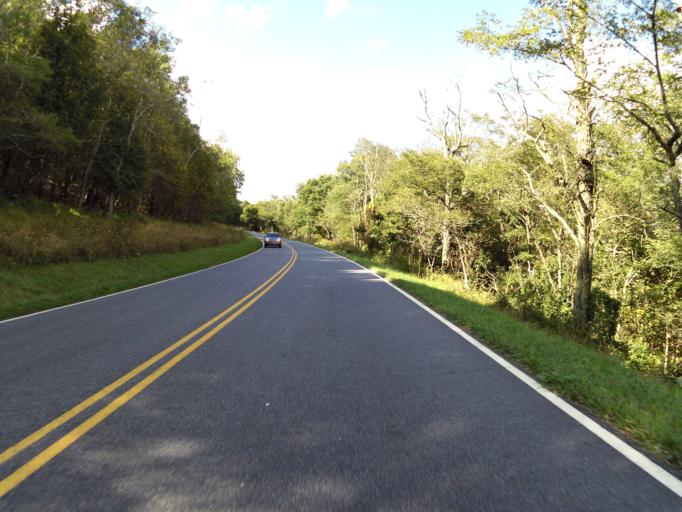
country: US
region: Virginia
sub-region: Page County
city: Luray
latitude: 38.5800
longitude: -78.3824
